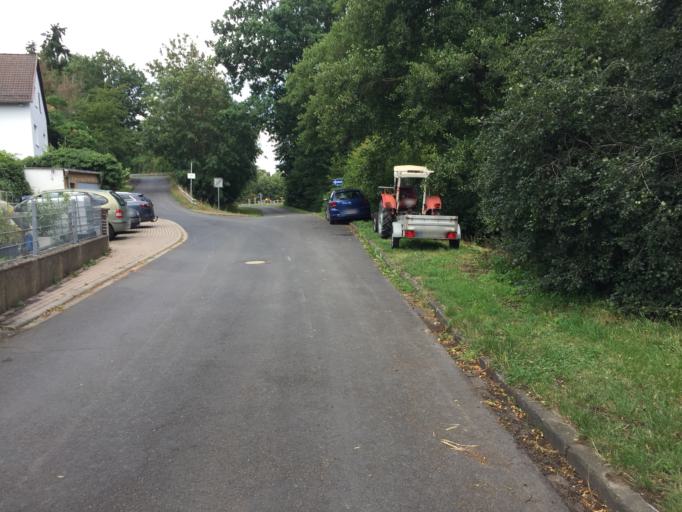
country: DE
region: Hesse
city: Schwalmstadt
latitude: 50.9163
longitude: 9.2580
